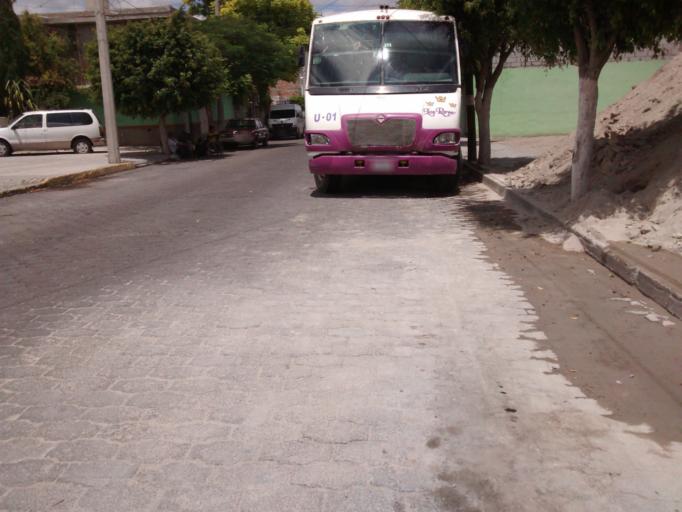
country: MX
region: Puebla
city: Tehuacan
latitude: 18.4563
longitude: -97.3886
